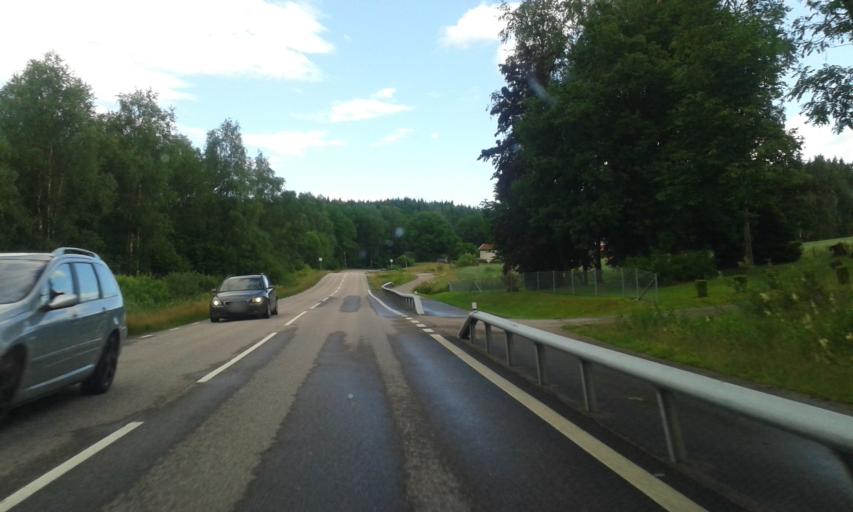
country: SE
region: Vaestra Goetaland
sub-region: Kungalvs Kommun
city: Diserod
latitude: 57.9050
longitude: 12.0081
